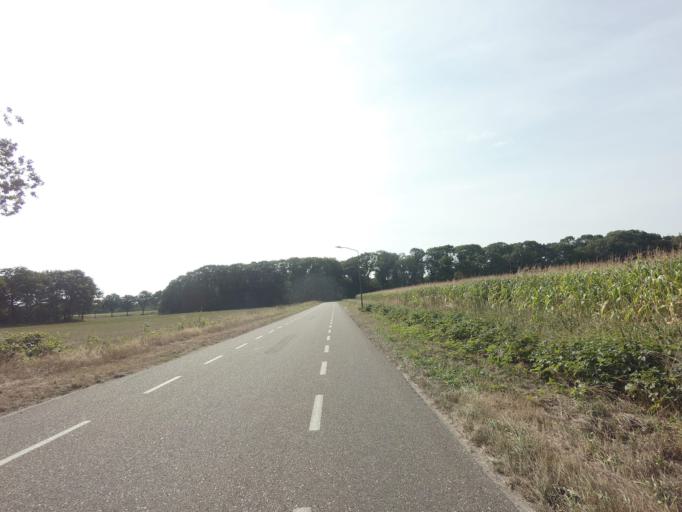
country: NL
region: North Brabant
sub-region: Gemeente Mill en Sint Hubert
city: Wilbertoord
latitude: 51.6370
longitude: 5.8189
